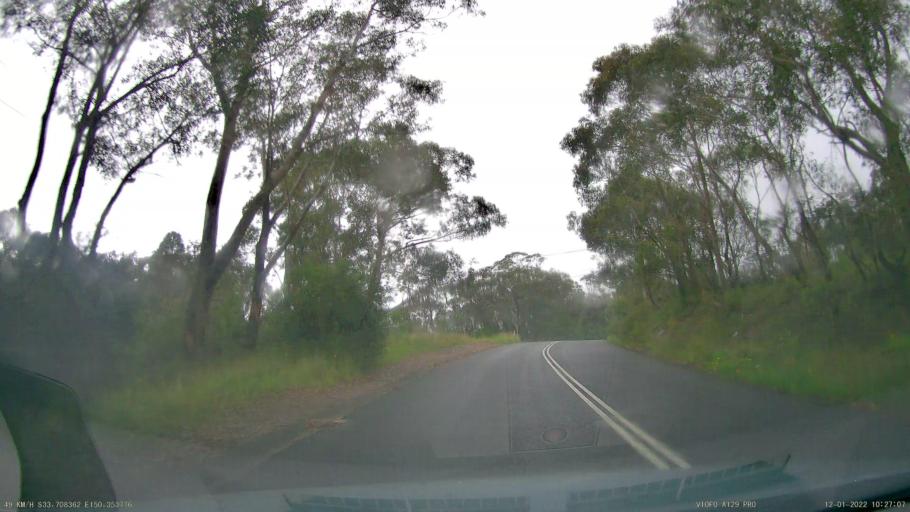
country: AU
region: New South Wales
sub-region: Blue Mountains Municipality
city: Leura
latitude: -33.7084
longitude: 150.3541
